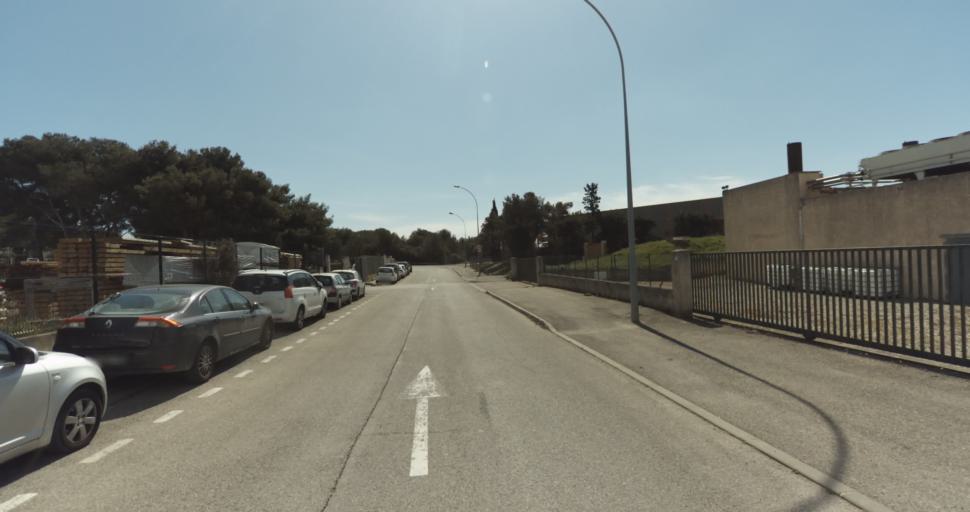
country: FR
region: Provence-Alpes-Cote d'Azur
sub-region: Departement des Bouches-du-Rhone
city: Lambesc
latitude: 43.6480
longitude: 5.2542
